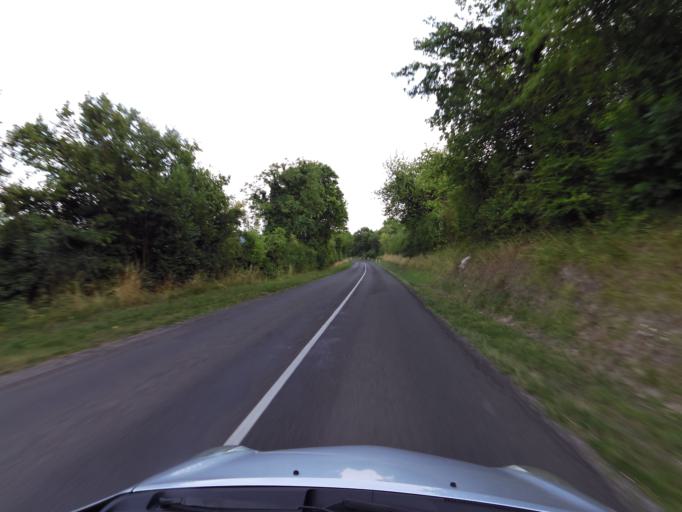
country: FR
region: Picardie
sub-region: Departement de l'Aisne
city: Bruyeres-et-Montberault
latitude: 49.4792
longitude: 3.6678
